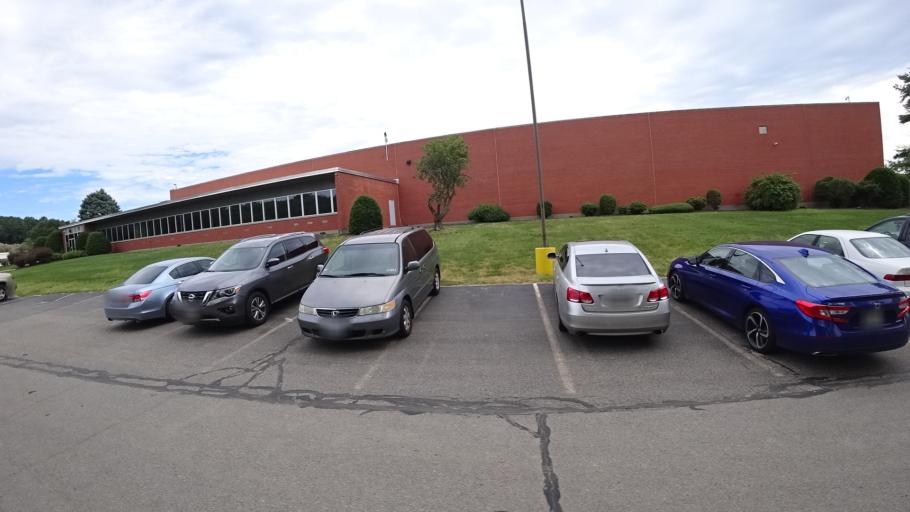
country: US
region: Massachusetts
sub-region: Norfolk County
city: Dedham
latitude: 42.2323
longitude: -71.1422
